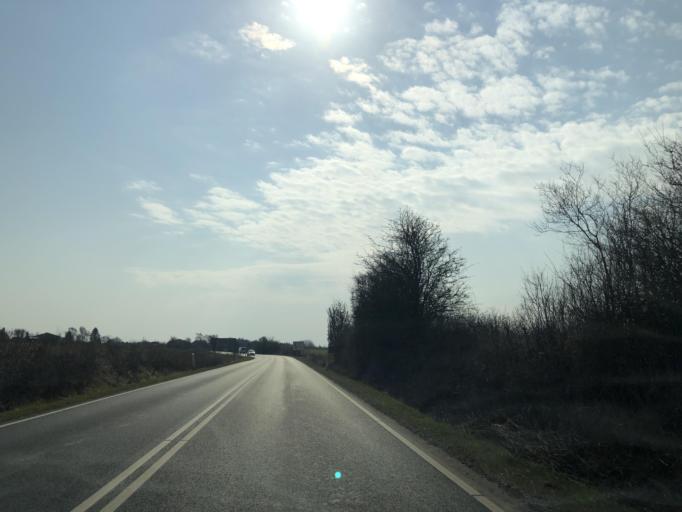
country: DK
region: South Denmark
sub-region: Sonderborg Kommune
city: Nordborg
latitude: 55.0380
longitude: 9.7525
